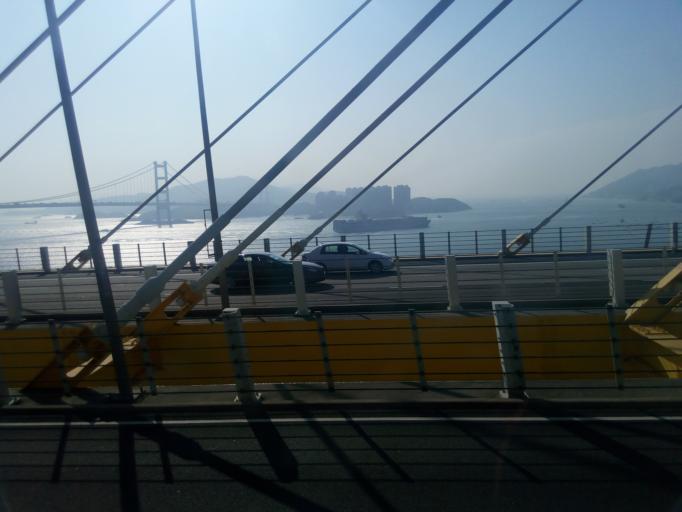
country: HK
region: Tsuen Wan
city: Tsuen Wan
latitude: 22.3629
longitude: 114.0804
